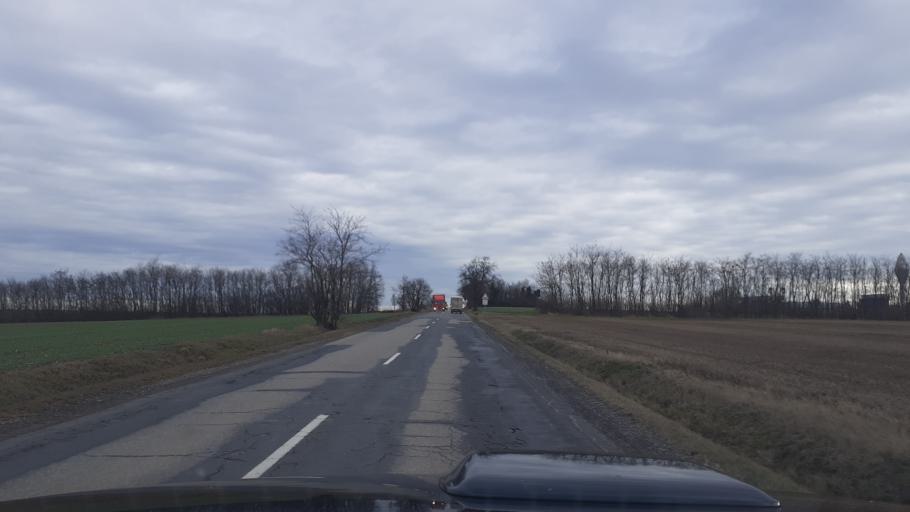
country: HU
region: Fejer
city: Mezofalva
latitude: 46.9469
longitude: 18.7421
